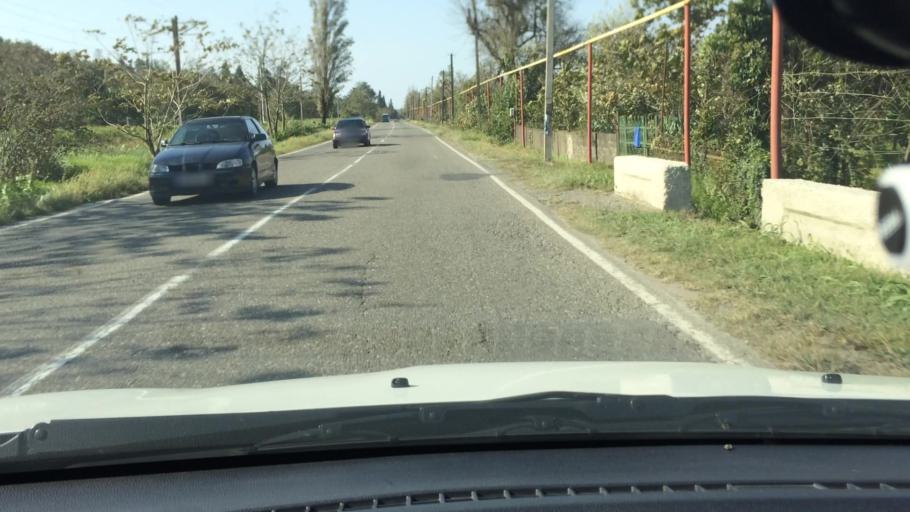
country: GE
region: Guria
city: Urek'i
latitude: 42.0578
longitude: 41.8478
